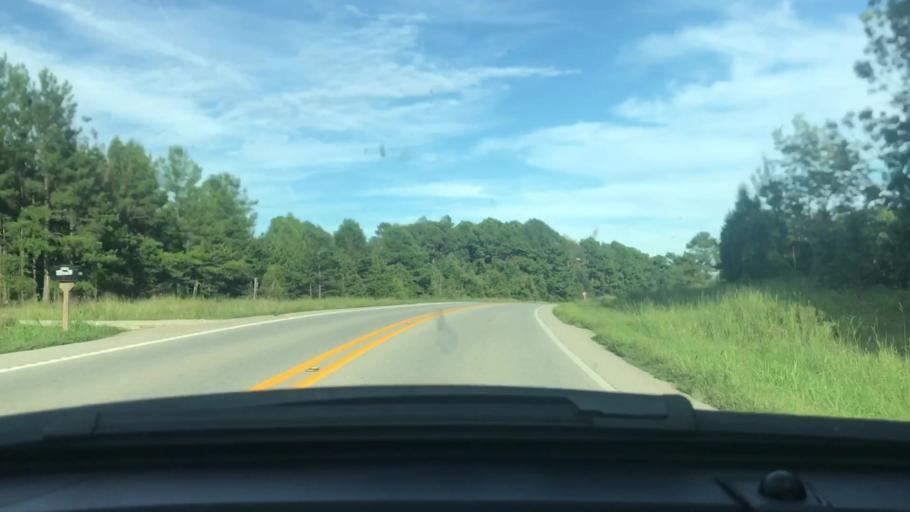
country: US
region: Arkansas
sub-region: Sharp County
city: Cherokee Village
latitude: 36.2769
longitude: -91.3119
